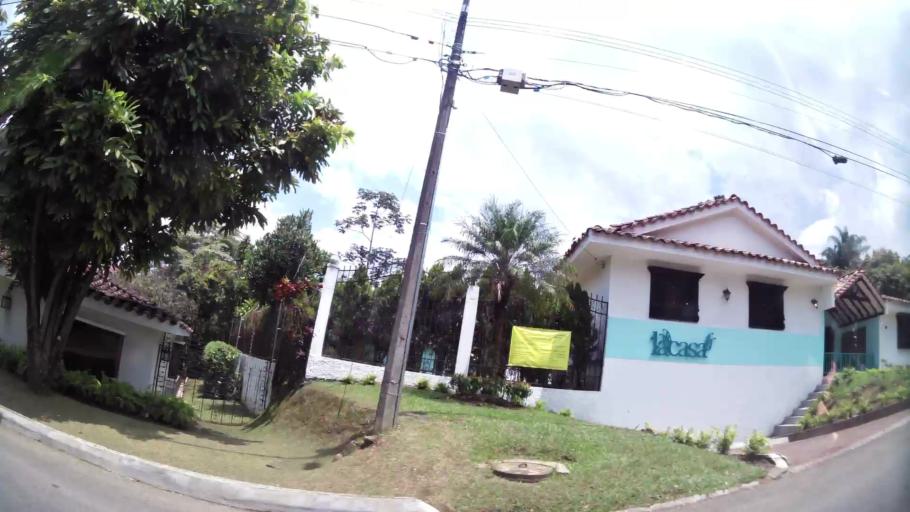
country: CO
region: Antioquia
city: Envigado
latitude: 6.1882
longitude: -75.5757
